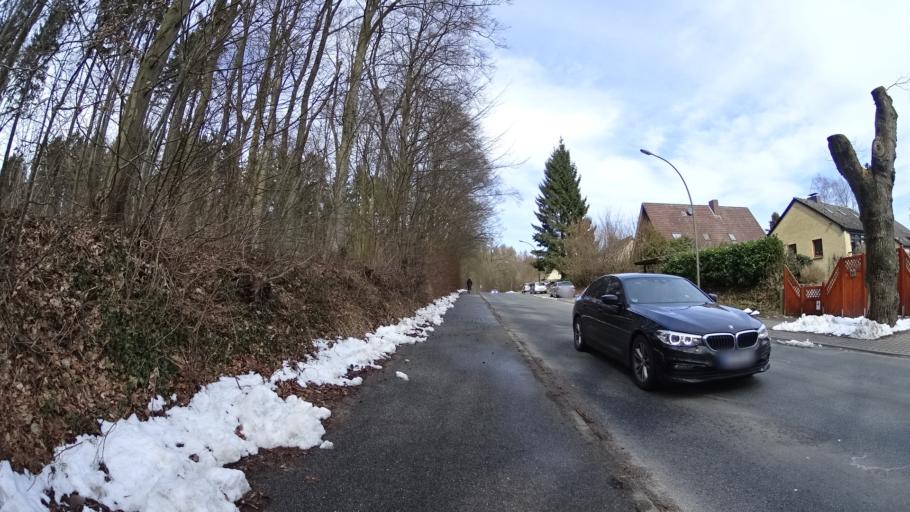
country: DE
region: Schleswig-Holstein
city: Kuhren
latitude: 54.2132
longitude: 10.2653
